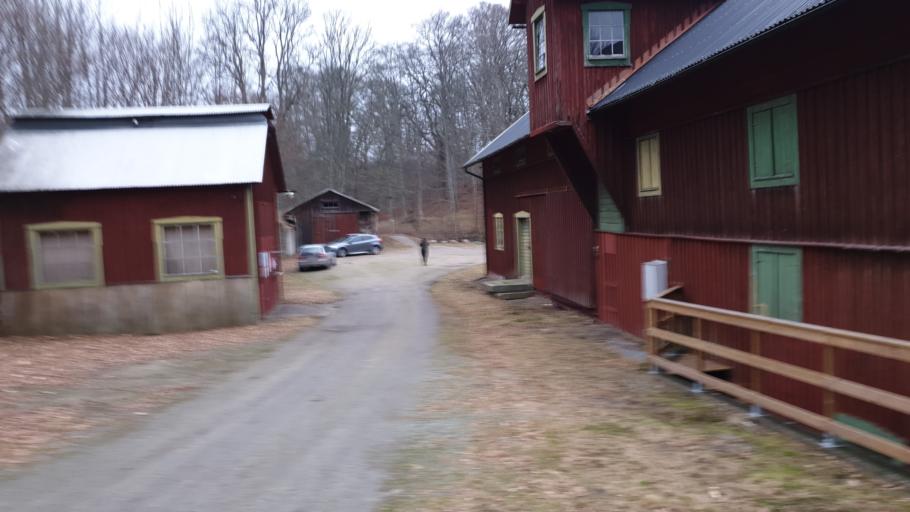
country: SE
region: Blekinge
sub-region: Karlskrona Kommun
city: Rodeby
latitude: 56.2170
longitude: 15.6731
